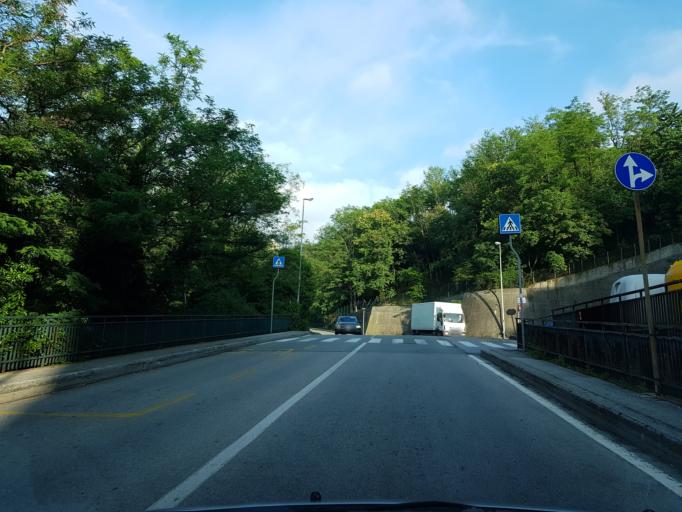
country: IT
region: Liguria
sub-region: Provincia di Genova
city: Genoa
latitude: 44.4526
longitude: 8.8989
